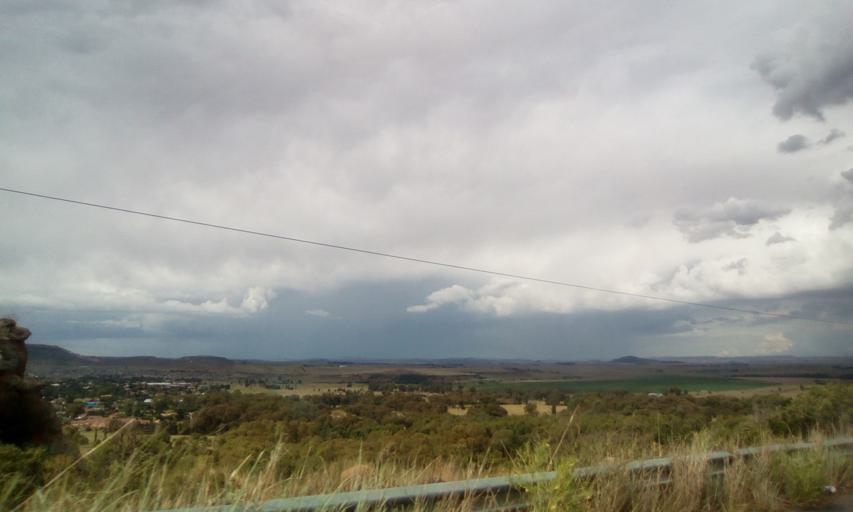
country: ZA
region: Orange Free State
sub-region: Thabo Mofutsanyana District Municipality
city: Ladybrand
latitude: -29.2124
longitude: 27.4572
